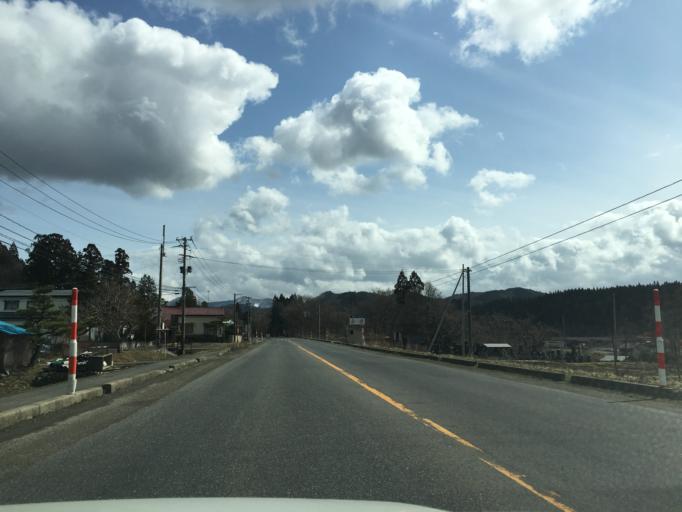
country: JP
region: Akita
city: Odate
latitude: 40.2266
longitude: 140.6002
